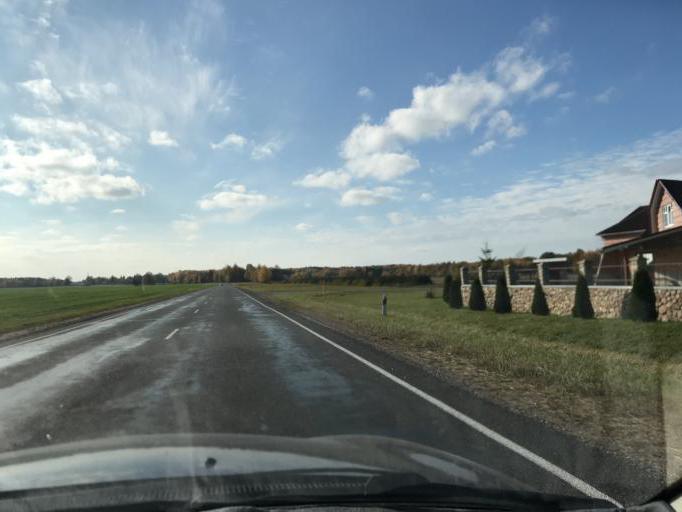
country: BY
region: Grodnenskaya
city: Voranava
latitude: 54.1878
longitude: 25.3408
